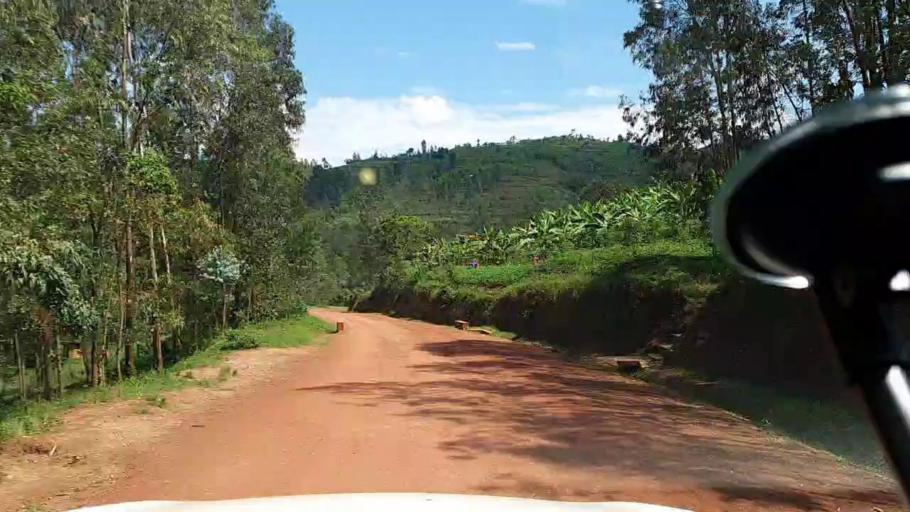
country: RW
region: Kigali
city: Kigali
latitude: -1.7965
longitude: 29.8868
